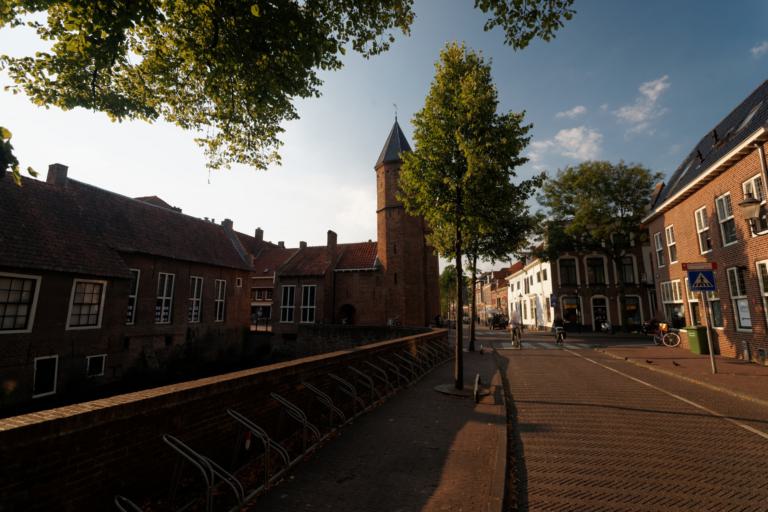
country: NL
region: Utrecht
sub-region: Gemeente Amersfoort
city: Amersfoort
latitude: 52.1569
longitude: 5.3933
